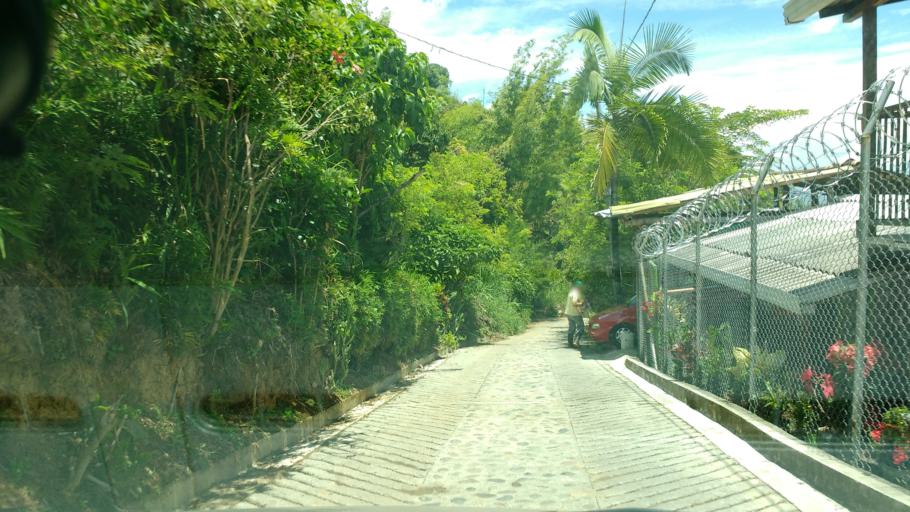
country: CO
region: Antioquia
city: Santa Barbara
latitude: 5.8584
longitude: -75.5578
